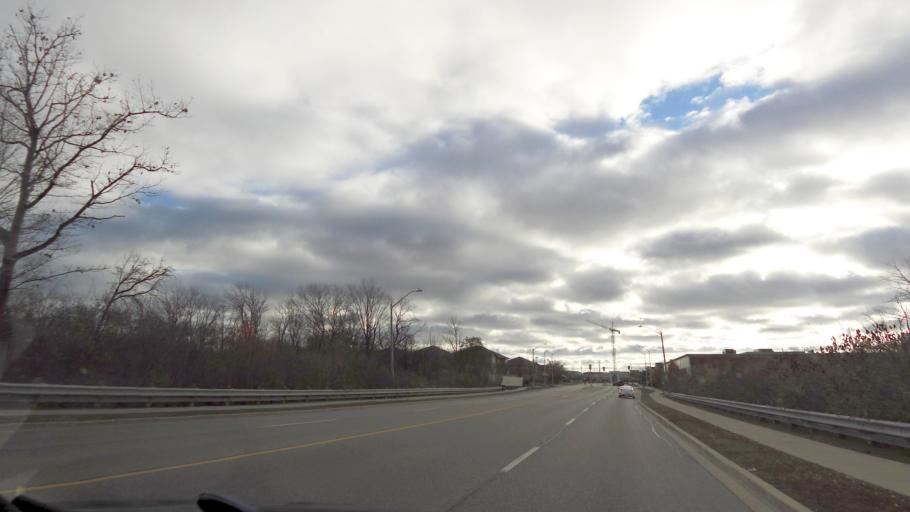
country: CA
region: Ontario
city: Oakville
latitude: 43.4868
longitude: -79.7130
